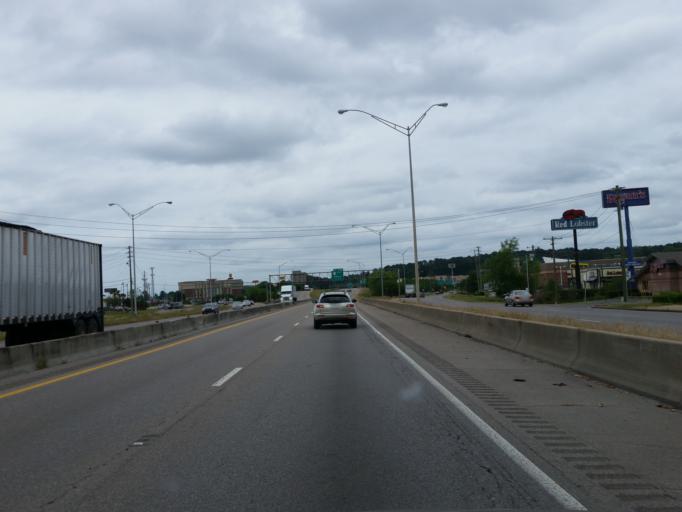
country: US
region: Mississippi
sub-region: Lauderdale County
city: Meridian
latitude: 32.3633
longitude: -88.6764
